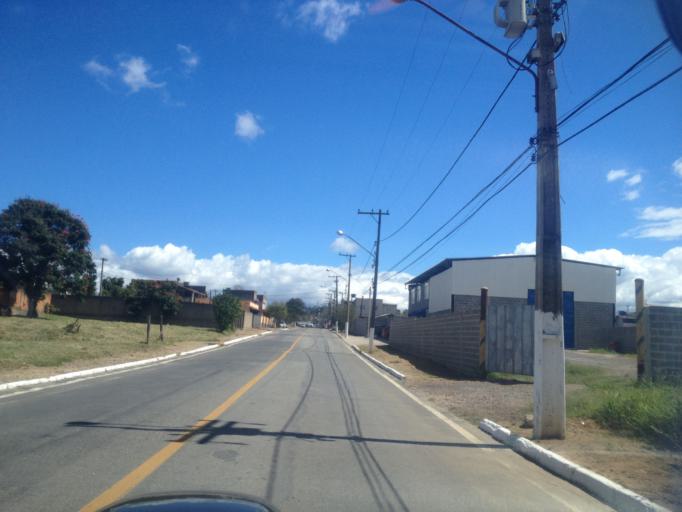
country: BR
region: Rio de Janeiro
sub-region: Porto Real
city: Porto Real
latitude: -22.4452
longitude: -44.3066
